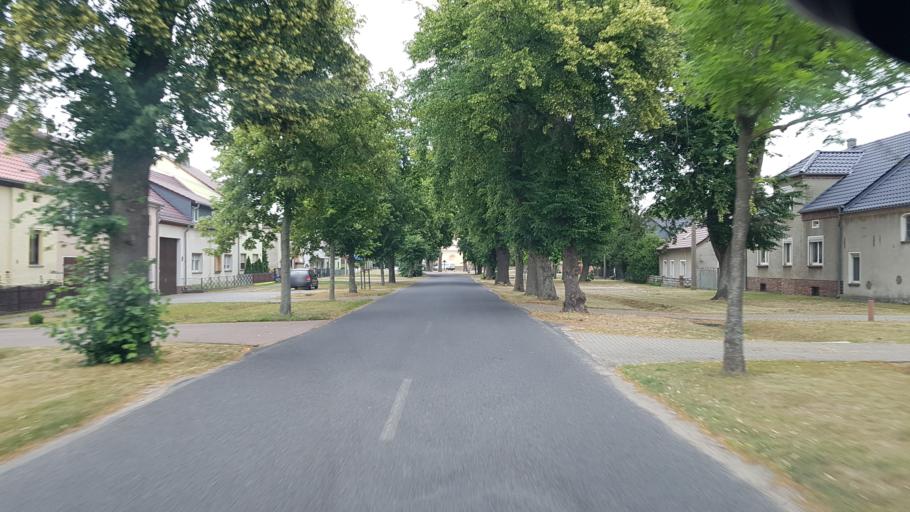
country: DE
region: Brandenburg
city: Golssen
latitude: 51.9495
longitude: 13.6404
